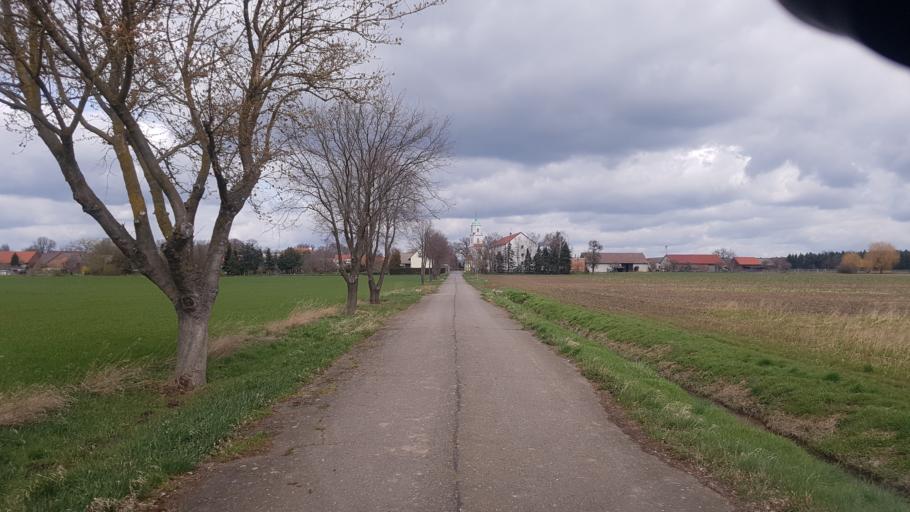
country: DE
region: Brandenburg
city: Hohenbucko
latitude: 51.6943
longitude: 13.4699
